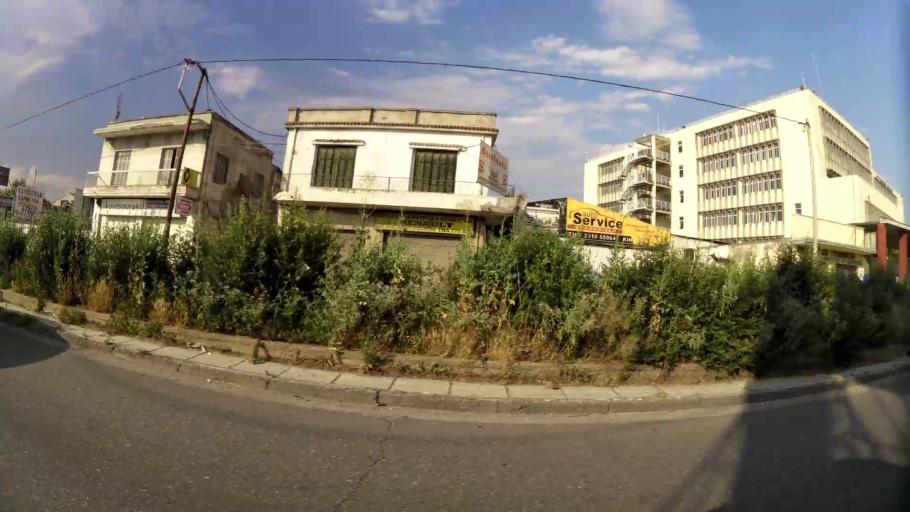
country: GR
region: Central Macedonia
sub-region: Nomos Thessalonikis
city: Menemeni
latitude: 40.6585
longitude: 22.9017
